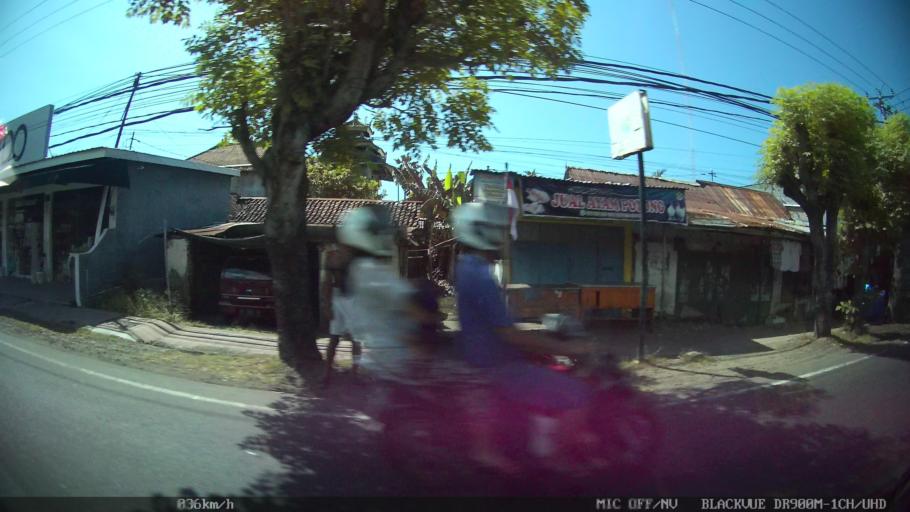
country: ID
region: Bali
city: Banjar Bunutpanggang
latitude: -8.1645
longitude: 115.0214
